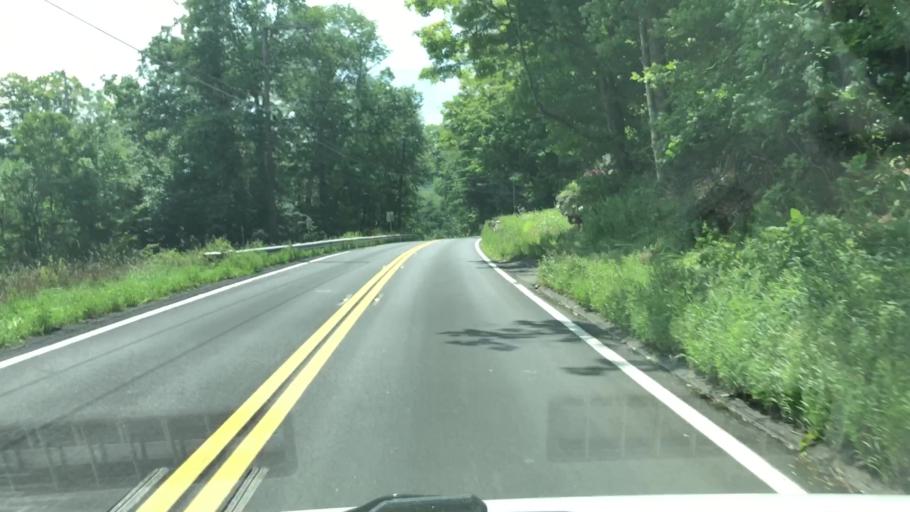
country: US
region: Massachusetts
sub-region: Franklin County
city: Ashfield
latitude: 42.5139
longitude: -72.7566
